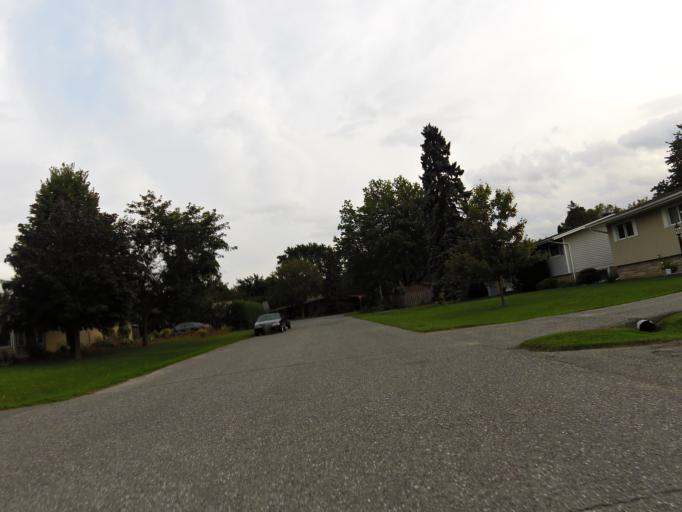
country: CA
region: Ontario
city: Bells Corners
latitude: 45.3174
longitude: -75.8158
